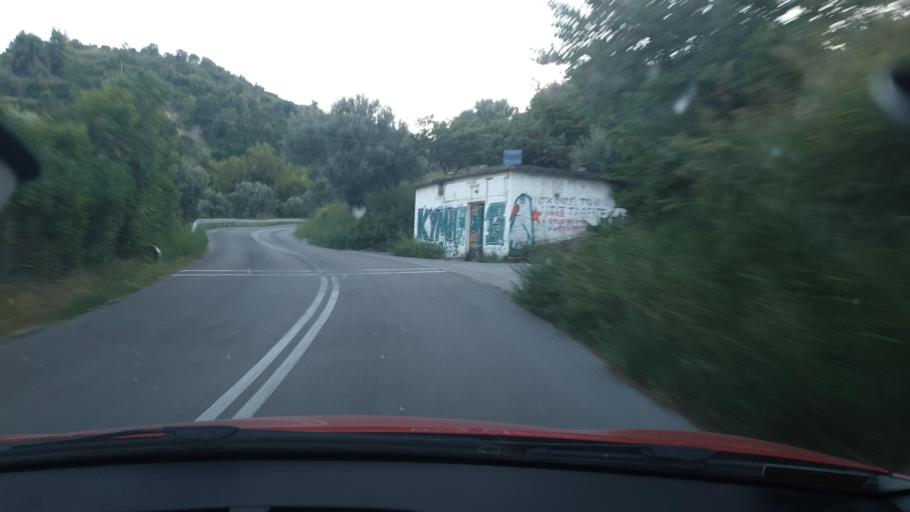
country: GR
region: Central Greece
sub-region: Nomos Evvoias
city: Kymi
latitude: 38.6311
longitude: 24.1192
